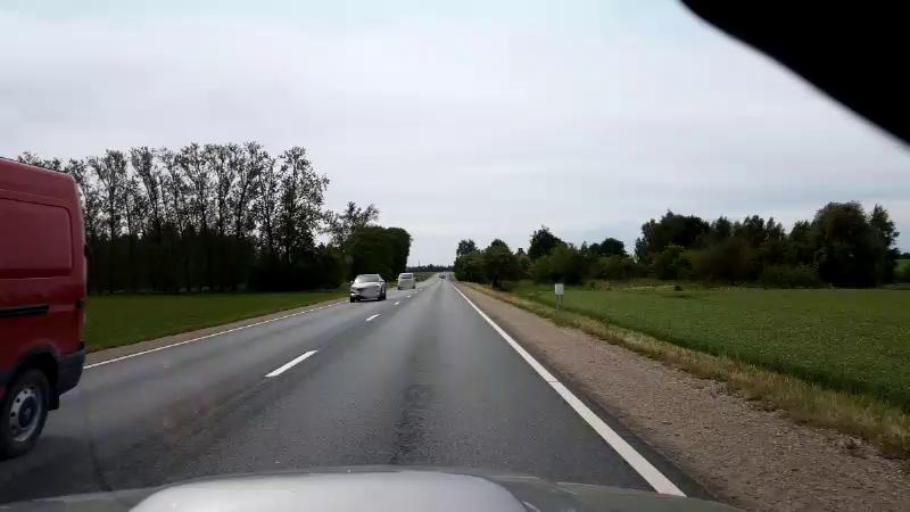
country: LV
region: Lecava
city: Iecava
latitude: 56.5435
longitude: 24.1733
